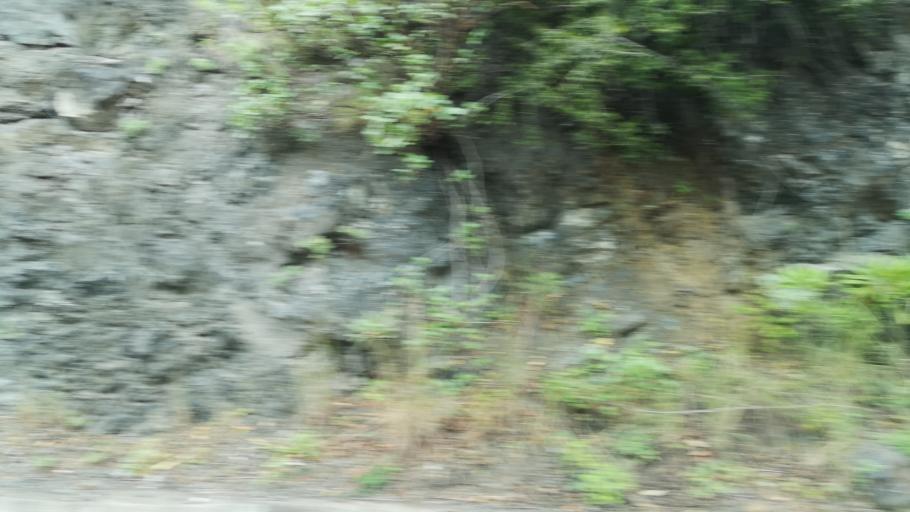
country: ES
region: Canary Islands
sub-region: Provincia de Santa Cruz de Tenerife
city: Hermigua
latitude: 28.1405
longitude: -17.1997
